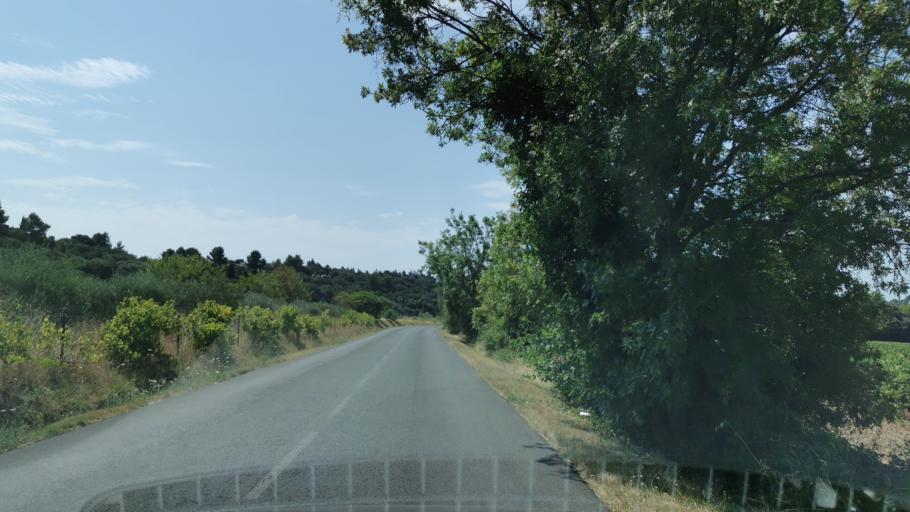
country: FR
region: Languedoc-Roussillon
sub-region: Departement de l'Aude
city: Bize-Minervois
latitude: 43.3074
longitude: 2.8711
